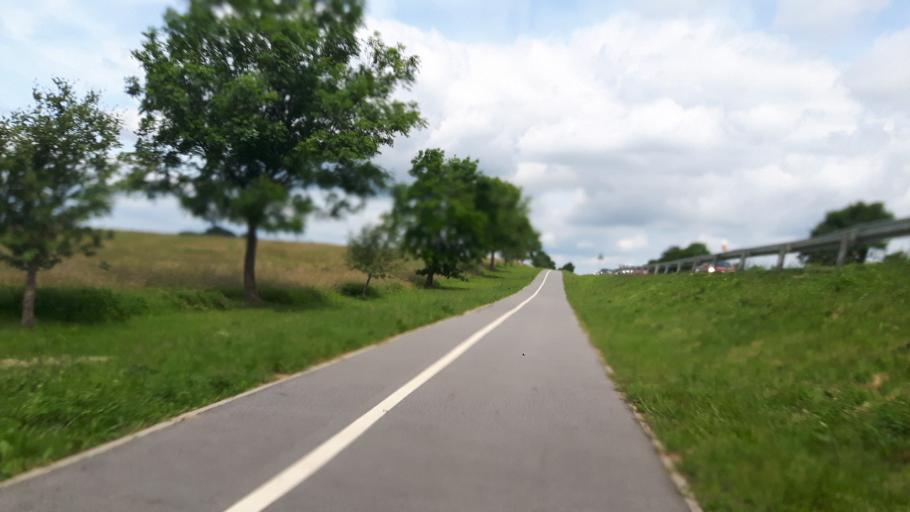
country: PL
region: West Pomeranian Voivodeship
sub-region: Powiat policki
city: Przeclaw
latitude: 53.3667
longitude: 14.4729
